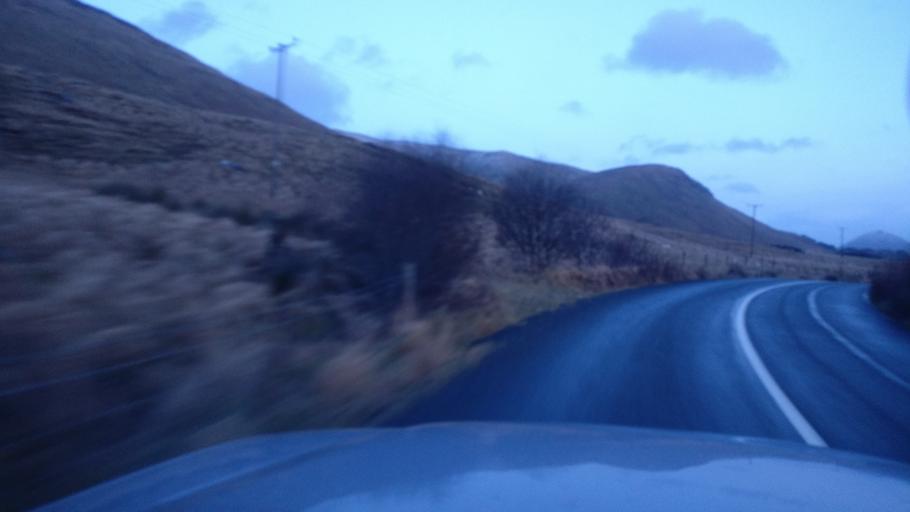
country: IE
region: Connaught
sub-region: Maigh Eo
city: Westport
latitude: 53.5564
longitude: -9.6422
